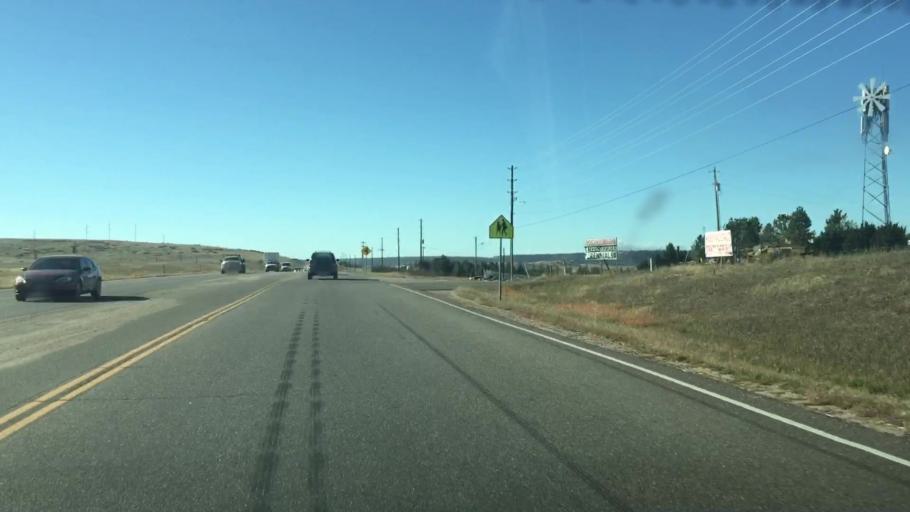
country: US
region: Colorado
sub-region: Douglas County
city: The Pinery
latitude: 39.4305
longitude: -104.7605
